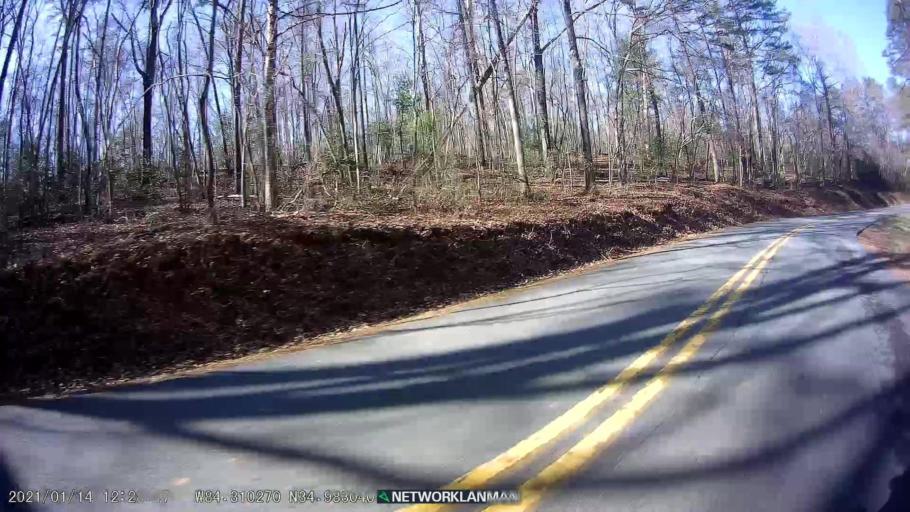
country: US
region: Georgia
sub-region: Fannin County
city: McCaysville
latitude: 34.9830
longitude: -84.3103
